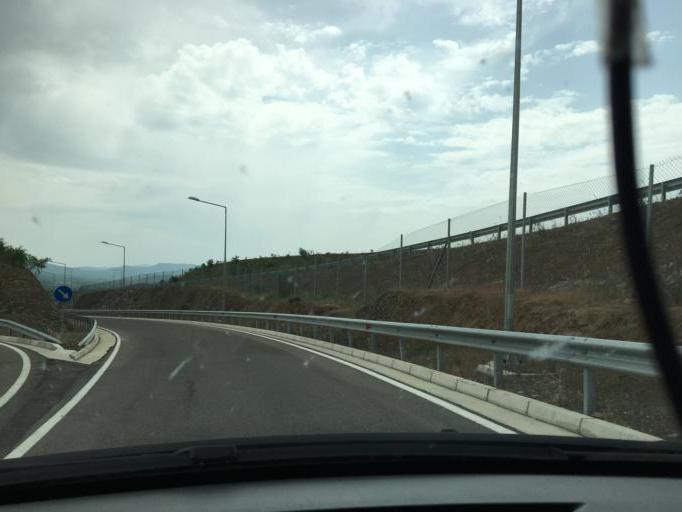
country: MK
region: Gevgelija
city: Miravci
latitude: 41.2961
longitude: 22.4306
